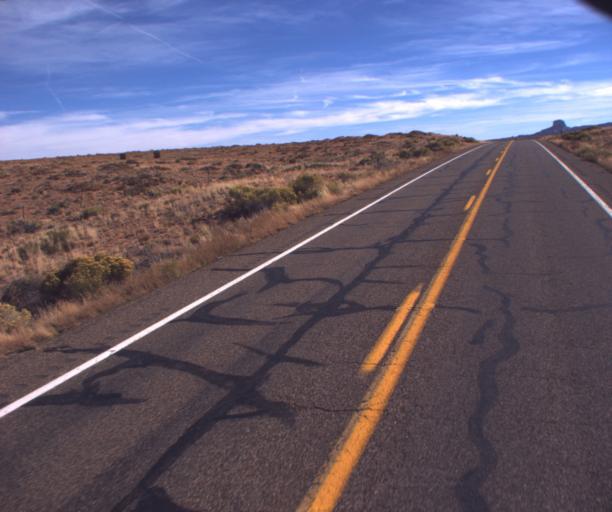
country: US
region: Arizona
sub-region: Coconino County
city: Kaibito
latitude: 36.6124
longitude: -111.0342
